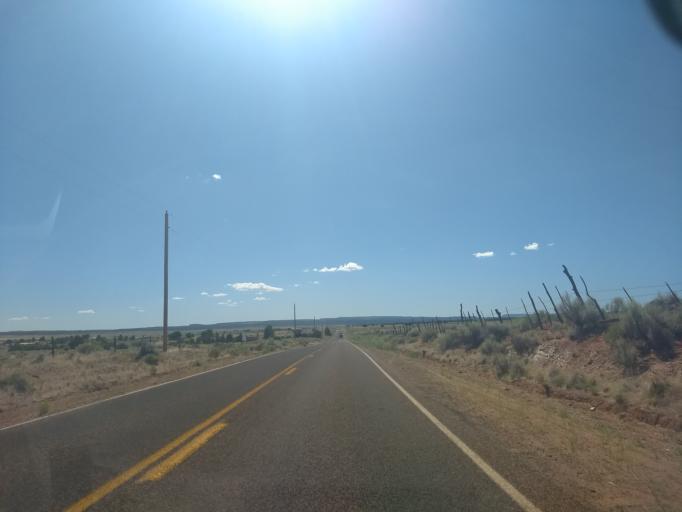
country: US
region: Arizona
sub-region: Mohave County
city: Colorado City
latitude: 36.9469
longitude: -112.9228
